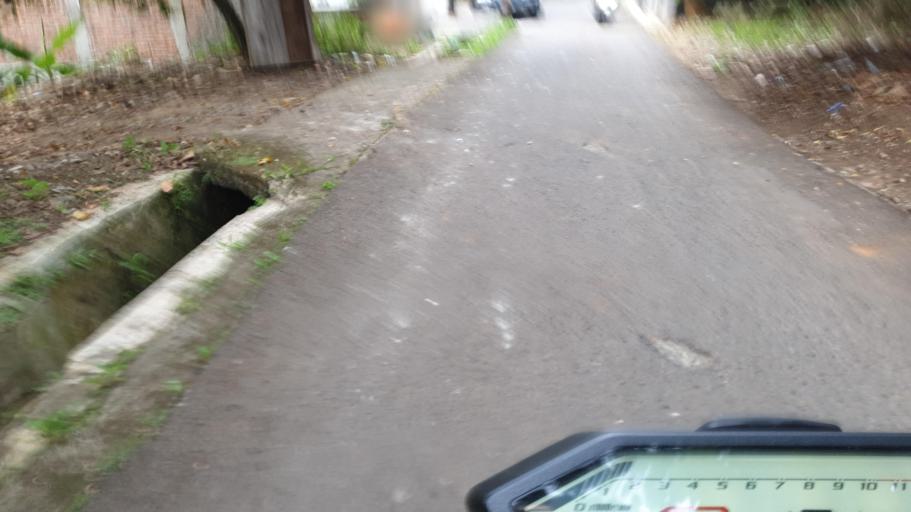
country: ID
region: West Java
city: Depok
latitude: -6.3644
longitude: 106.8386
